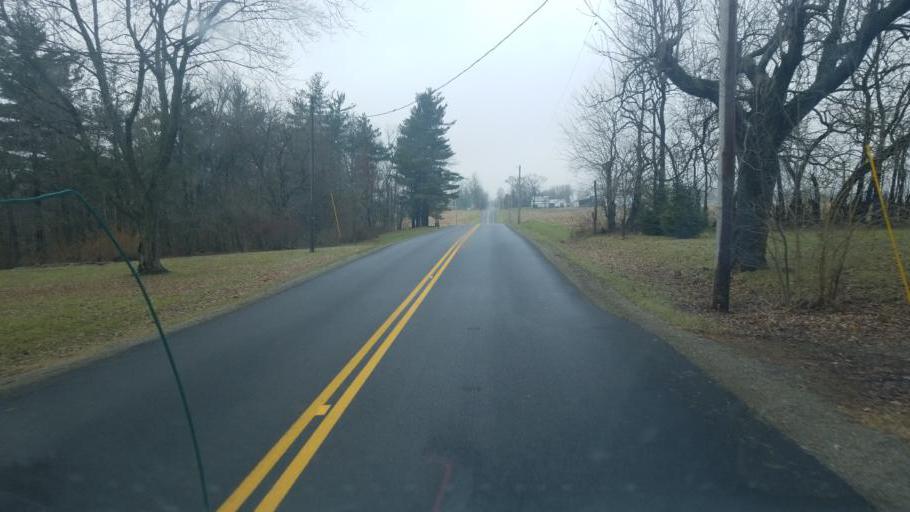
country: US
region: Ohio
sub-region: Champaign County
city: North Lewisburg
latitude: 40.2876
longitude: -83.5769
